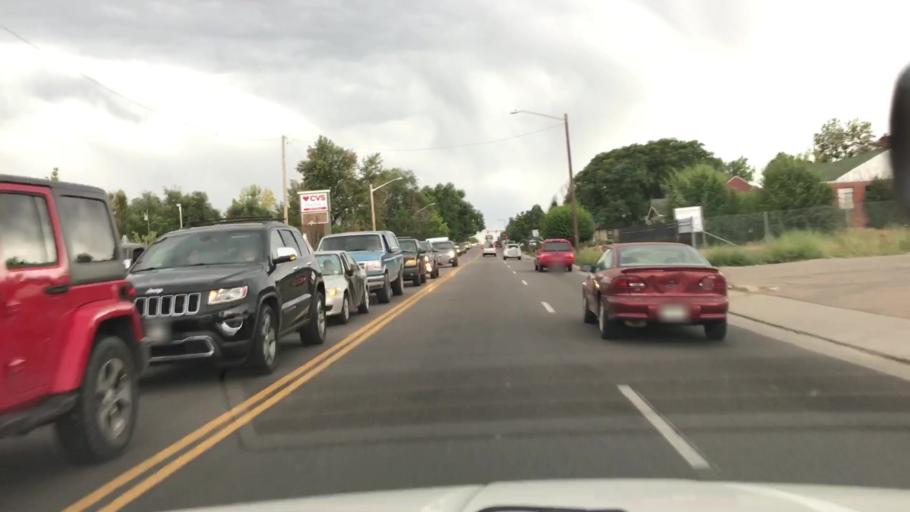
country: US
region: Colorado
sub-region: Jefferson County
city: Edgewater
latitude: 39.7691
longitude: -105.0534
